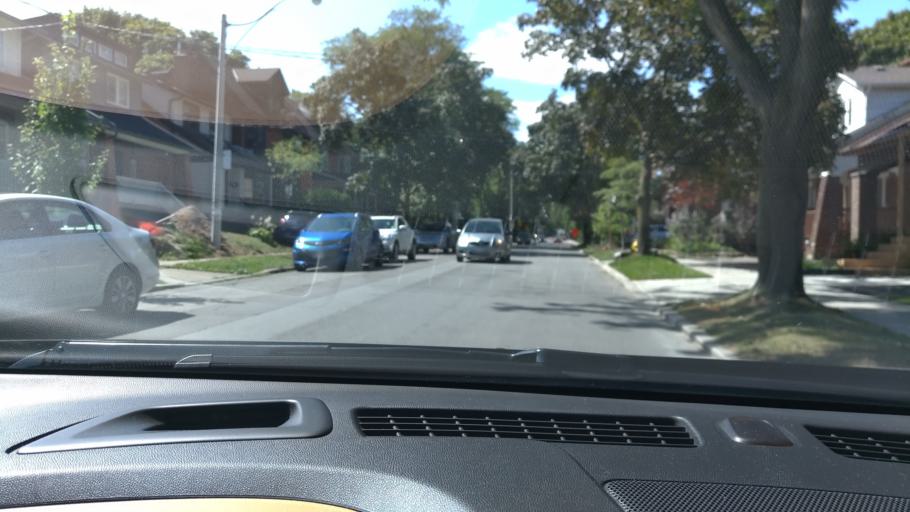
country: CA
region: Ontario
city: Toronto
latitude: 43.7031
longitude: -79.3990
